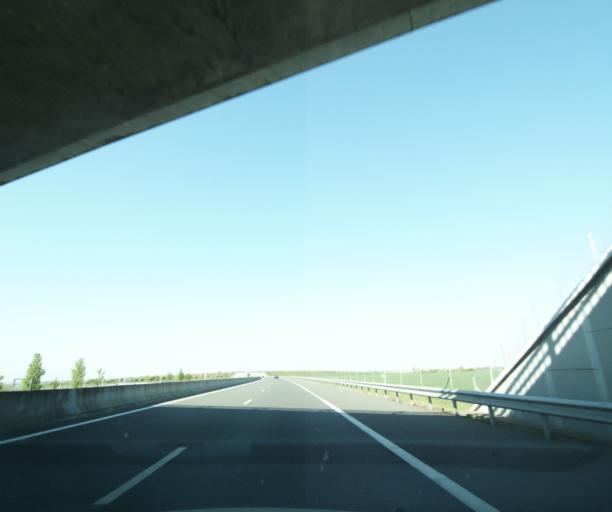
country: FR
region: Centre
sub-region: Departement du Loiret
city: Ascheres-le-Marche
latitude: 48.0985
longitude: 2.0313
